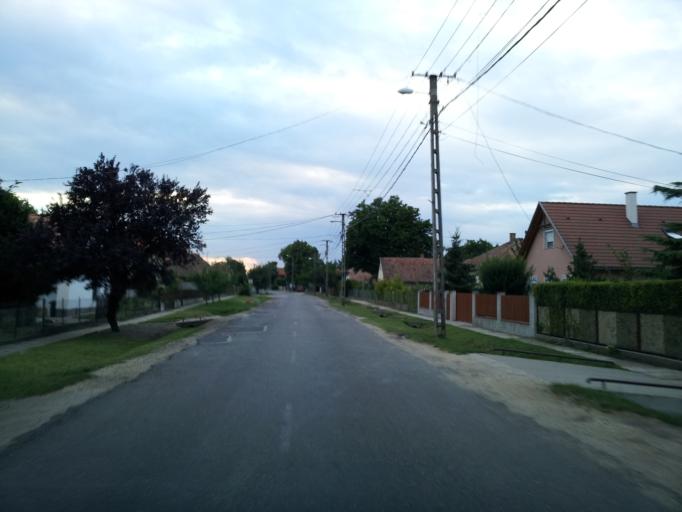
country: HU
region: Somogy
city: Balatonszabadi
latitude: 46.8862
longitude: 18.1453
